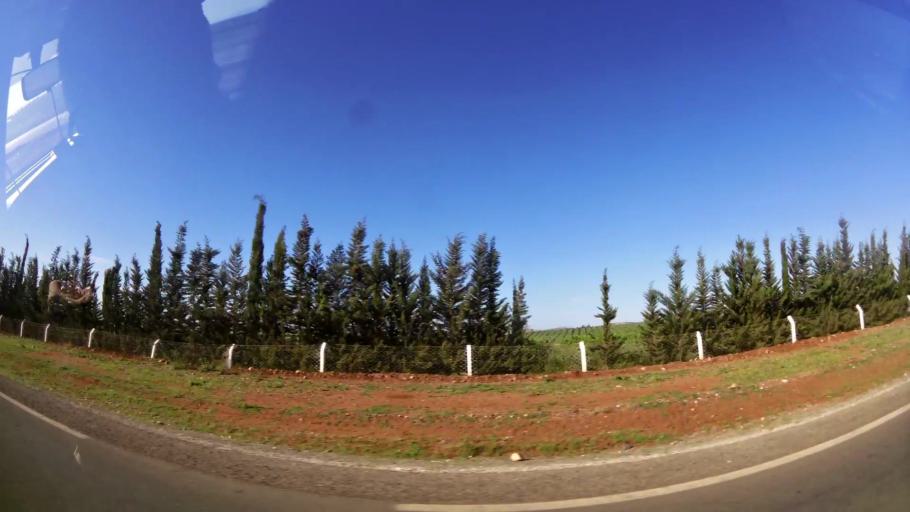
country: MA
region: Oriental
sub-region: Berkane-Taourirt
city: Ahfir
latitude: 34.9967
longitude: -2.1682
